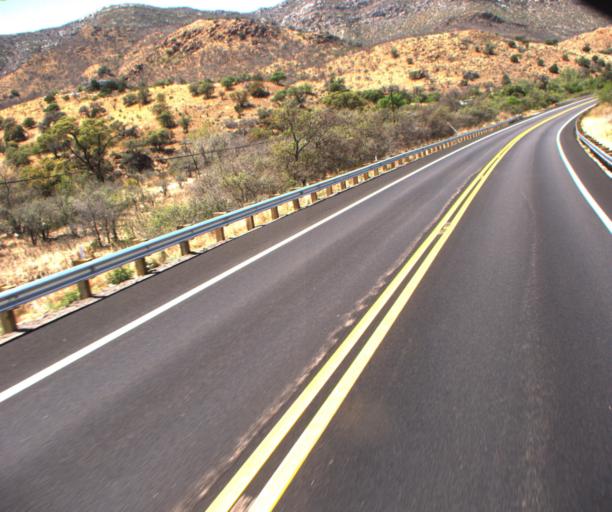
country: US
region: Arizona
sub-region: Cochise County
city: Bisbee
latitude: 31.4979
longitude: -109.9995
